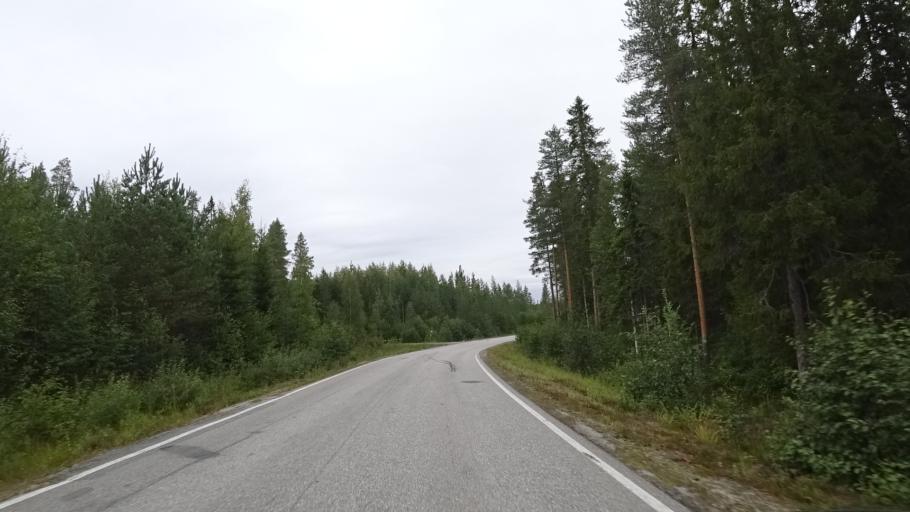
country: FI
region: North Karelia
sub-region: Pielisen Karjala
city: Lieksa
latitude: 63.3568
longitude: 30.2614
